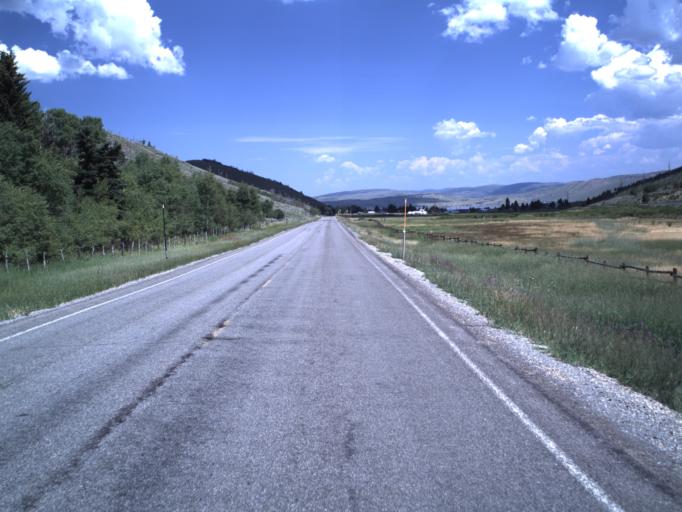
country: US
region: Utah
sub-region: Sanpete County
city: Fairview
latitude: 39.7101
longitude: -111.1632
